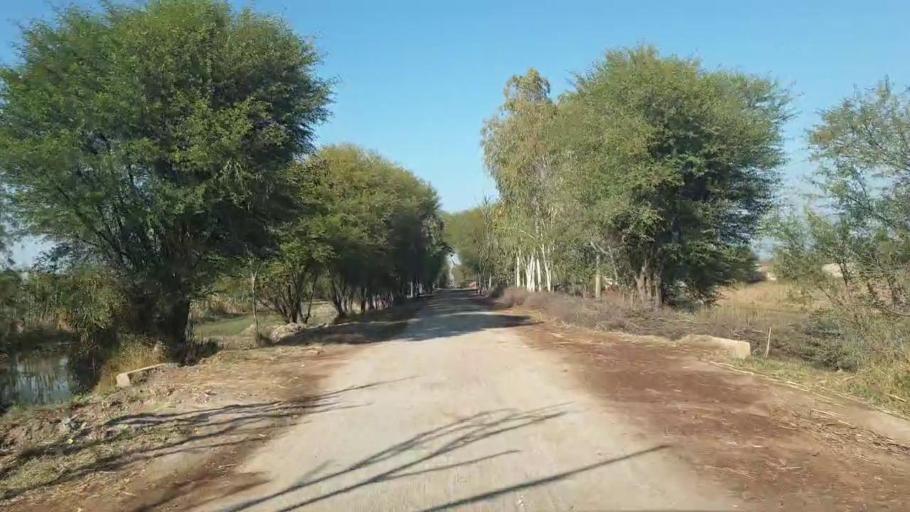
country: PK
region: Sindh
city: Shahdadpur
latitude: 25.9246
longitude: 68.5301
